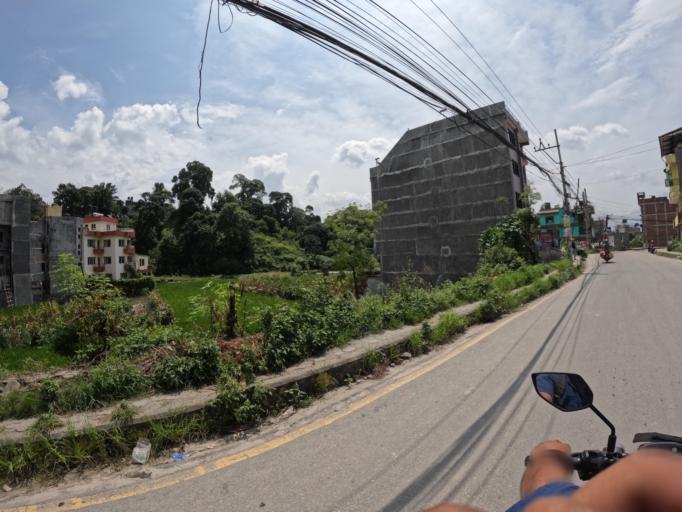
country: NP
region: Central Region
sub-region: Bagmati Zone
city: Bhaktapur
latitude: 27.6759
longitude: 85.3822
